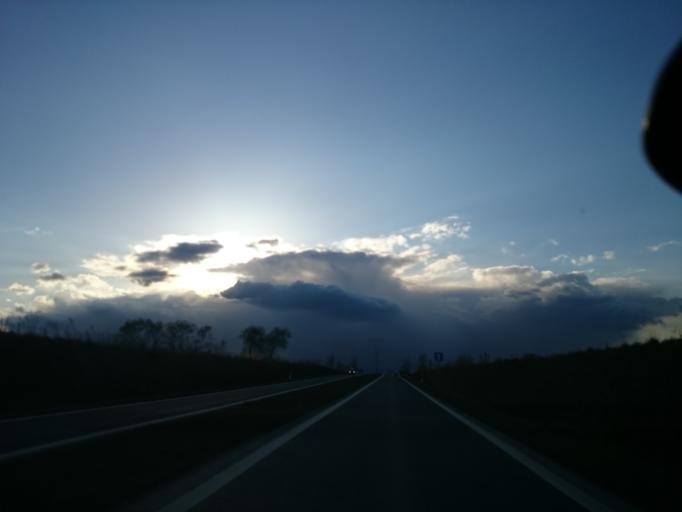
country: PL
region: Lower Silesian Voivodeship
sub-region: Powiat zabkowicki
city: Zabkowice Slaskie
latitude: 50.5786
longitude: 16.8110
